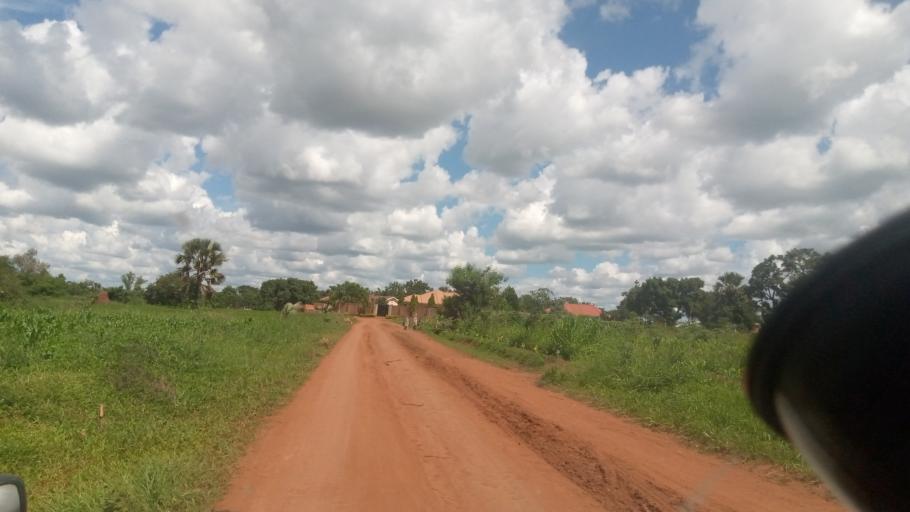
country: UG
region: Northern Region
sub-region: Lira District
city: Lira
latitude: 2.2343
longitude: 32.9078
